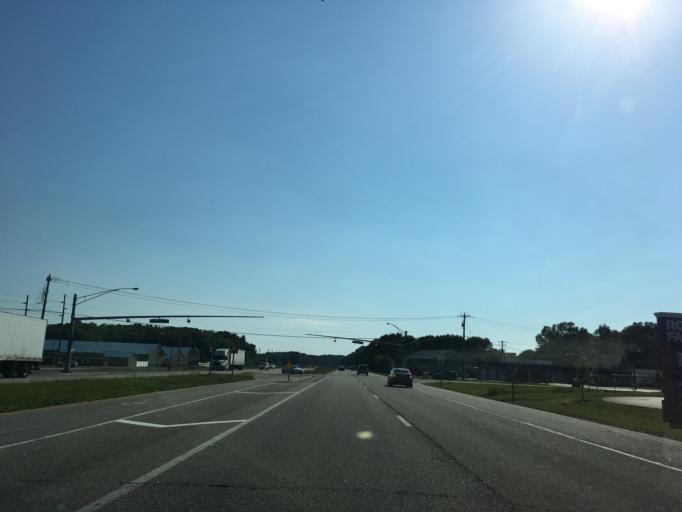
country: US
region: Maryland
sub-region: Queen Anne's County
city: Grasonville
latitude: 38.9881
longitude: -76.1518
